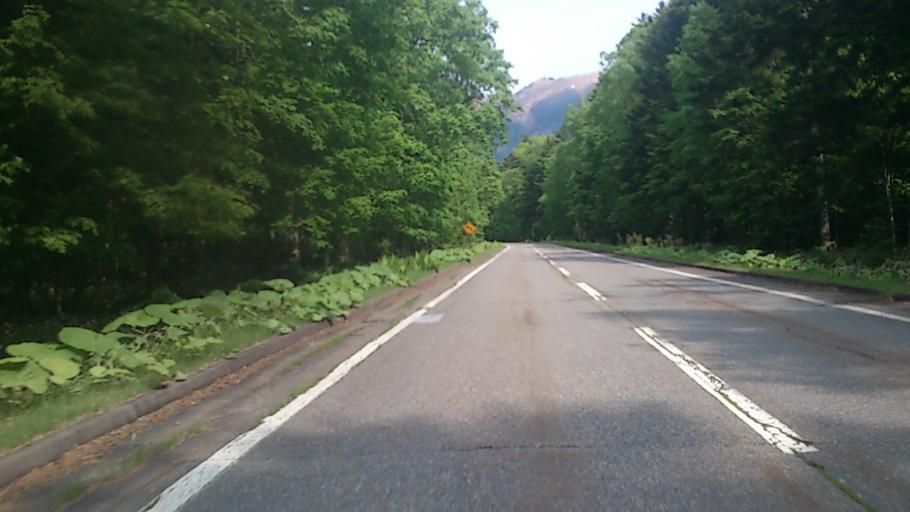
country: JP
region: Hokkaido
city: Kitami
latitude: 43.4032
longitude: 143.9652
